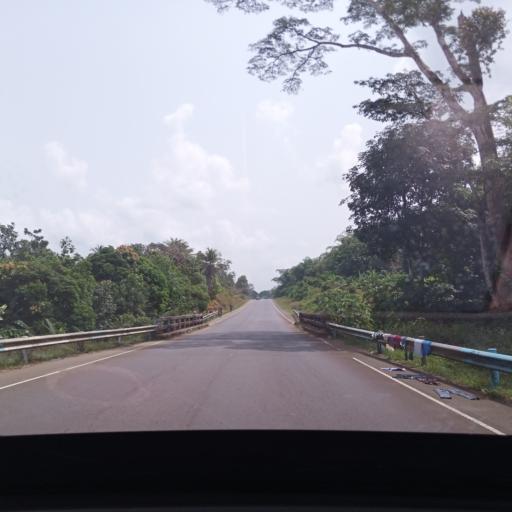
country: LR
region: Margibi
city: Kakata
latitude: 6.2524
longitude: -10.3015
